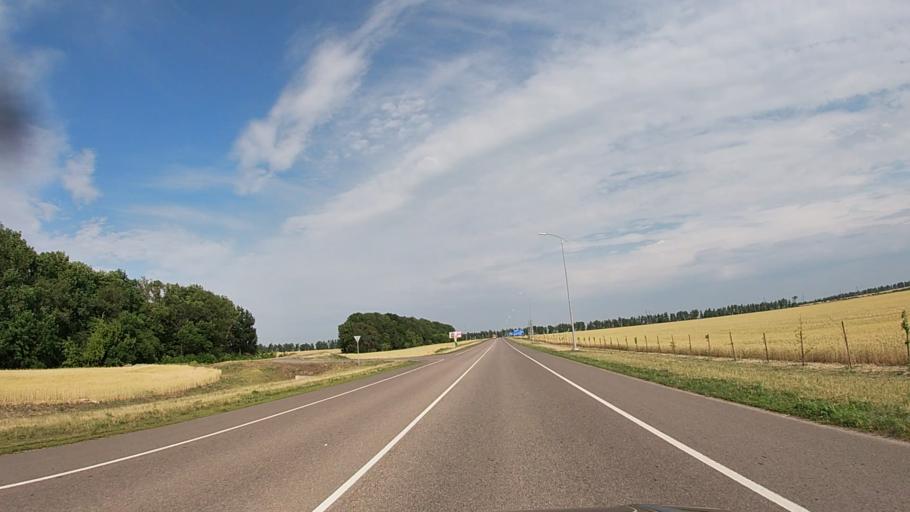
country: RU
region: Belgorod
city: Proletarskiy
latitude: 50.8281
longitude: 35.7747
